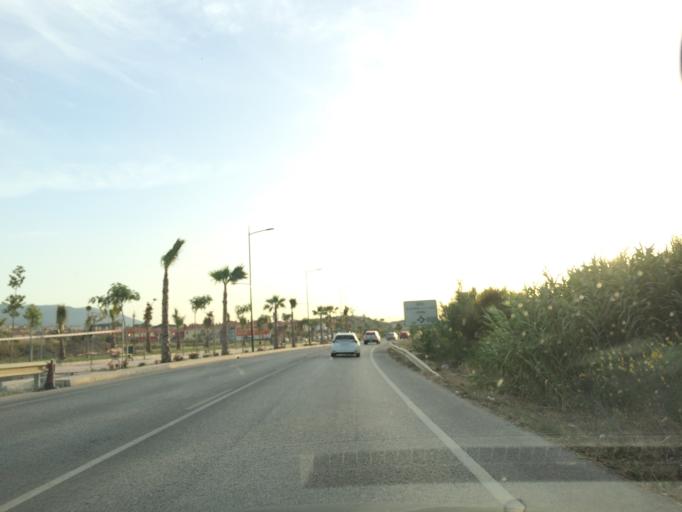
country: ES
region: Andalusia
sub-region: Provincia de Malaga
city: Alhaurin de la Torre
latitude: 36.6683
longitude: -4.5439
